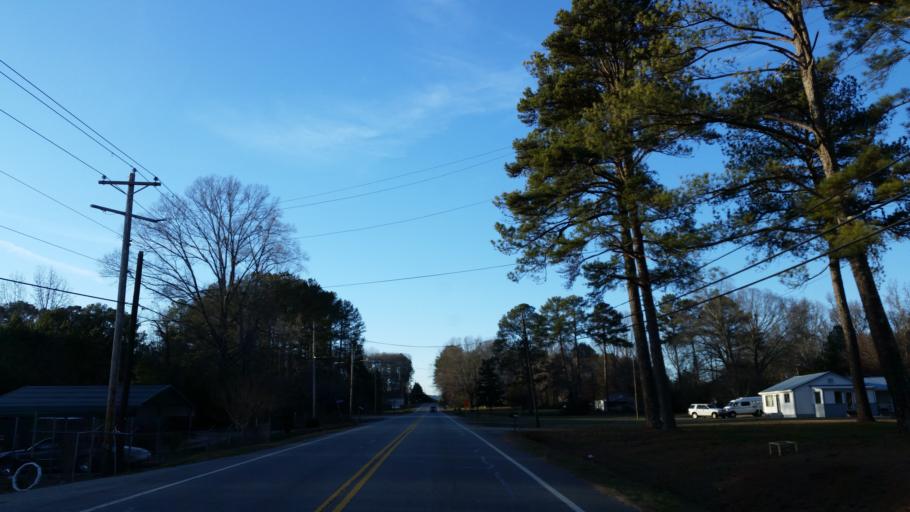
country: US
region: Georgia
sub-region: Whitfield County
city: Dalton
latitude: 34.6497
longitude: -84.9736
